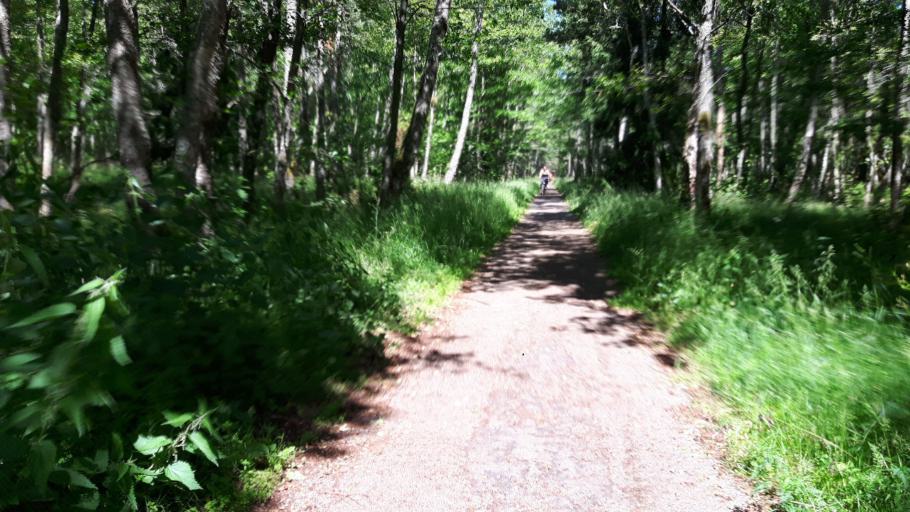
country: LT
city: Neringa
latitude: 55.4316
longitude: 21.0750
